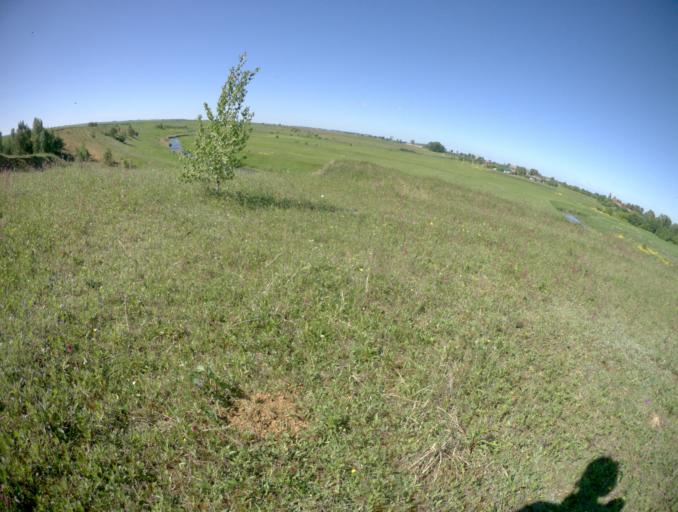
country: RU
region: Ivanovo
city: Gavrilov Posad
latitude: 56.5311
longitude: 40.2014
